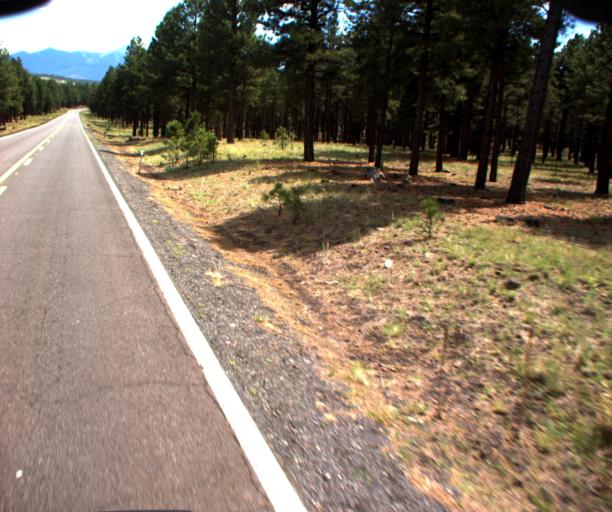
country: US
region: Arizona
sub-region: Coconino County
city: Parks
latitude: 35.4633
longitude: -111.7819
